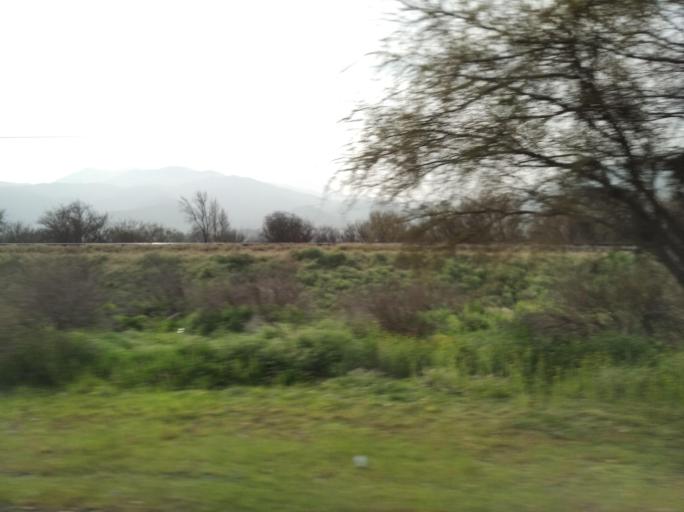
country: CL
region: Santiago Metropolitan
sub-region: Provincia de Chacabuco
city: Lampa
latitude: -33.1275
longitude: -70.9225
